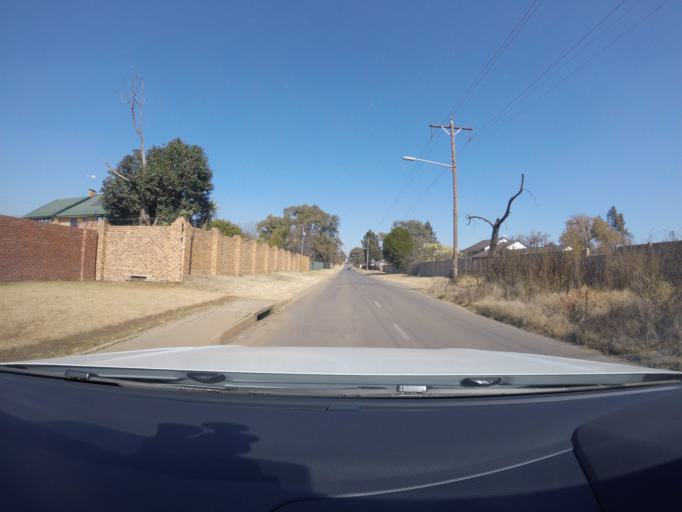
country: ZA
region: Gauteng
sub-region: Ekurhuleni Metropolitan Municipality
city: Benoni
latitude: -26.1224
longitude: 28.3004
